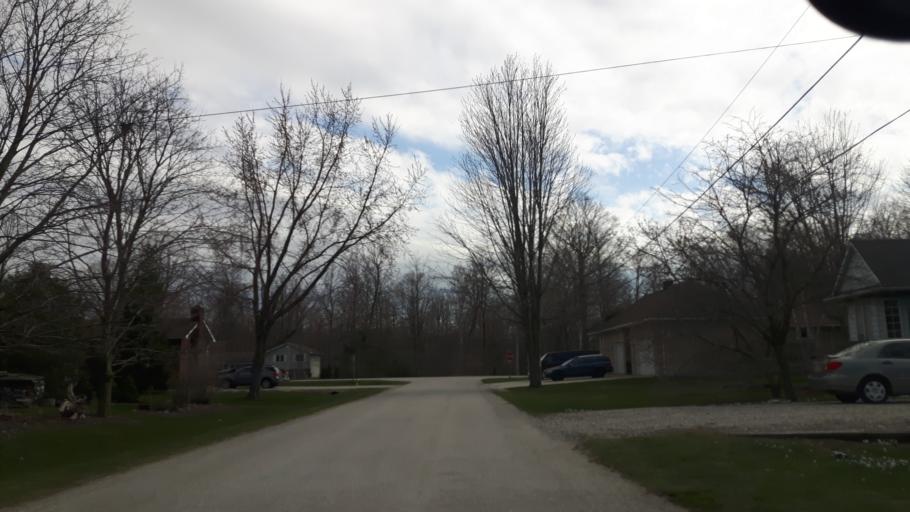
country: CA
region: Ontario
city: Bluewater
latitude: 43.5575
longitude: -81.6953
